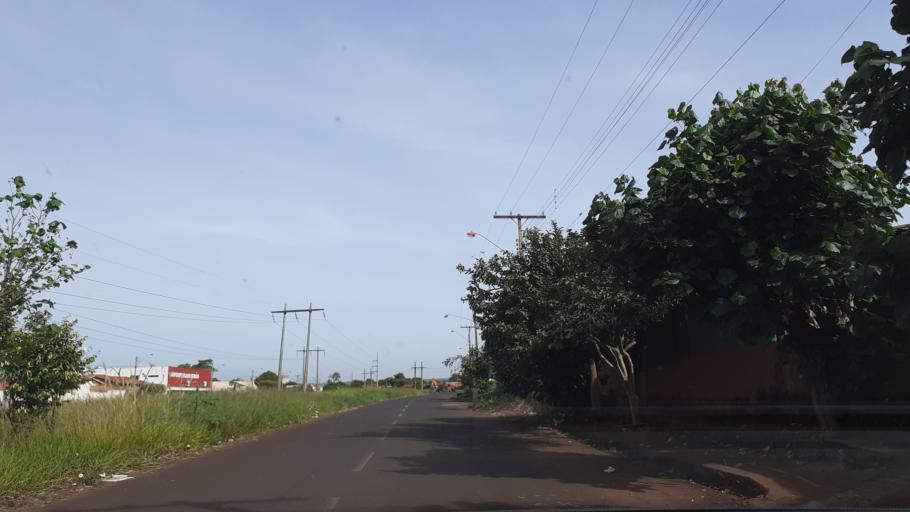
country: BR
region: Goias
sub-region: Itumbiara
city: Itumbiara
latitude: -18.4192
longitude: -49.2426
